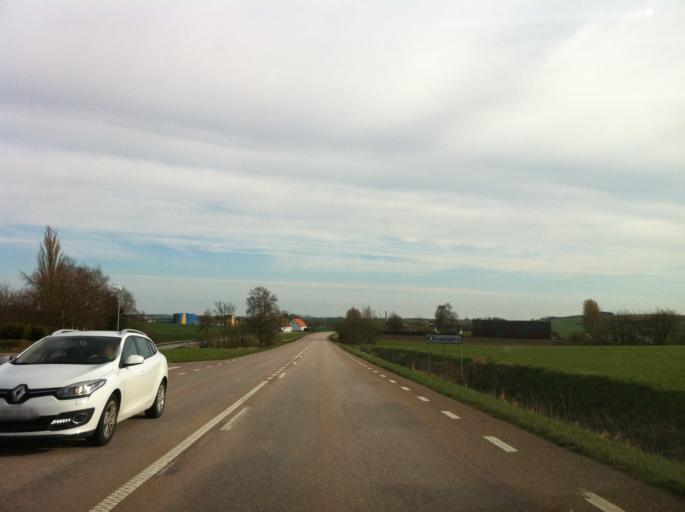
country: SE
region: Skane
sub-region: Landskrona
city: Asmundtorp
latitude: 55.9458
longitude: 12.9486
